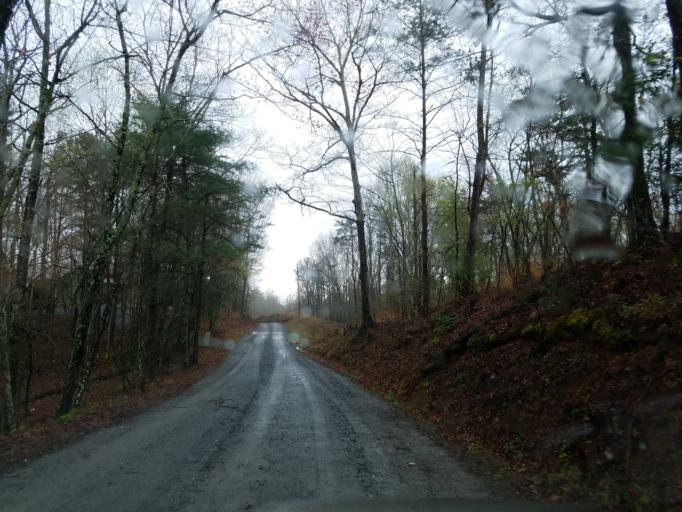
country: US
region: Georgia
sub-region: Fannin County
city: Blue Ridge
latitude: 34.8446
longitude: -84.2342
